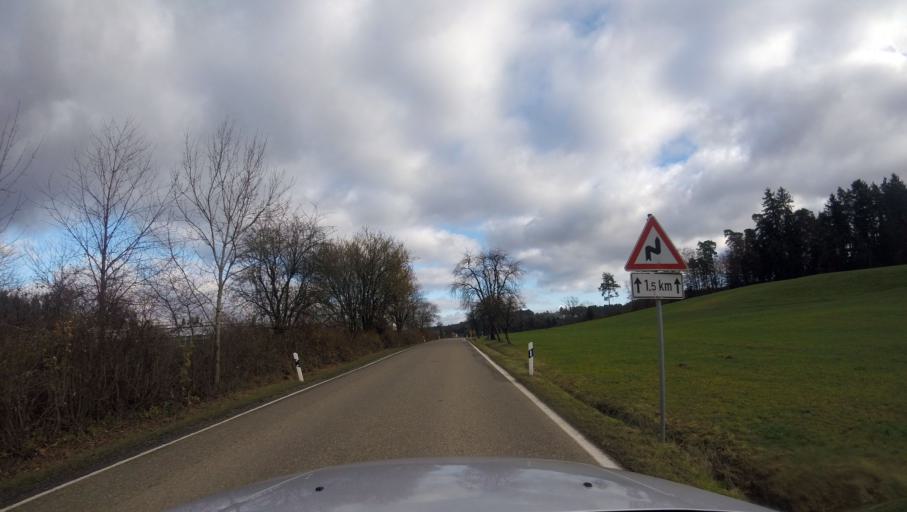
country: DE
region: Baden-Wuerttemberg
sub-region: Regierungsbezirk Stuttgart
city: Fichtenberg
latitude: 48.9484
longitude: 9.7013
